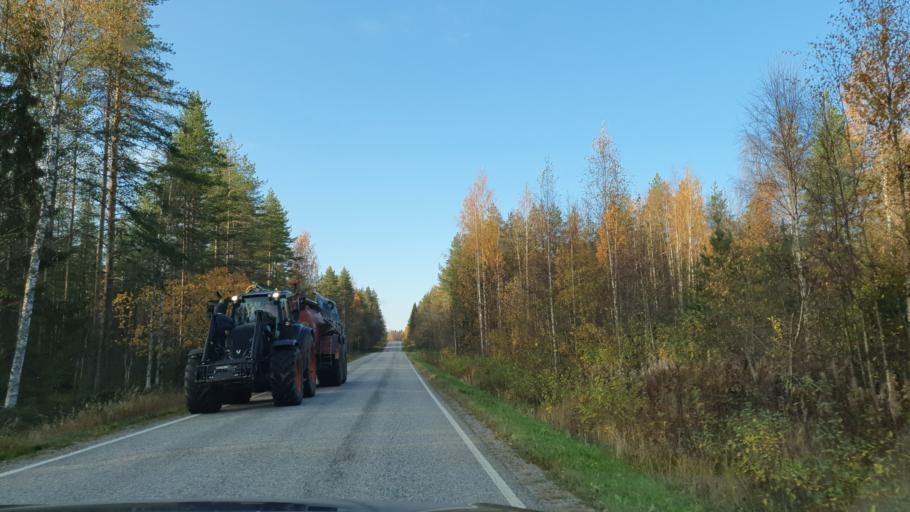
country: FI
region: Kainuu
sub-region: Kehys-Kainuu
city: Kuhmo
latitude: 64.2024
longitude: 29.4503
